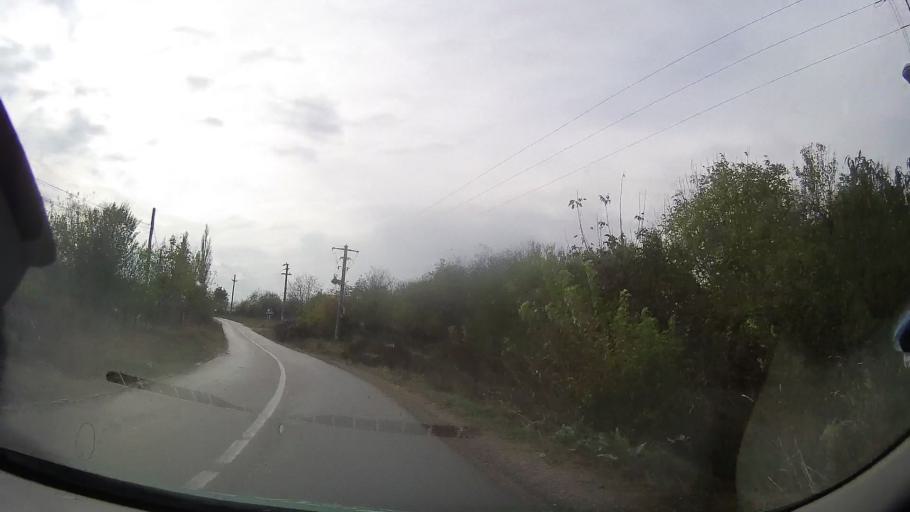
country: RO
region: Ialomita
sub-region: Comuna Maia
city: Maia
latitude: 44.7282
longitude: 26.3940
